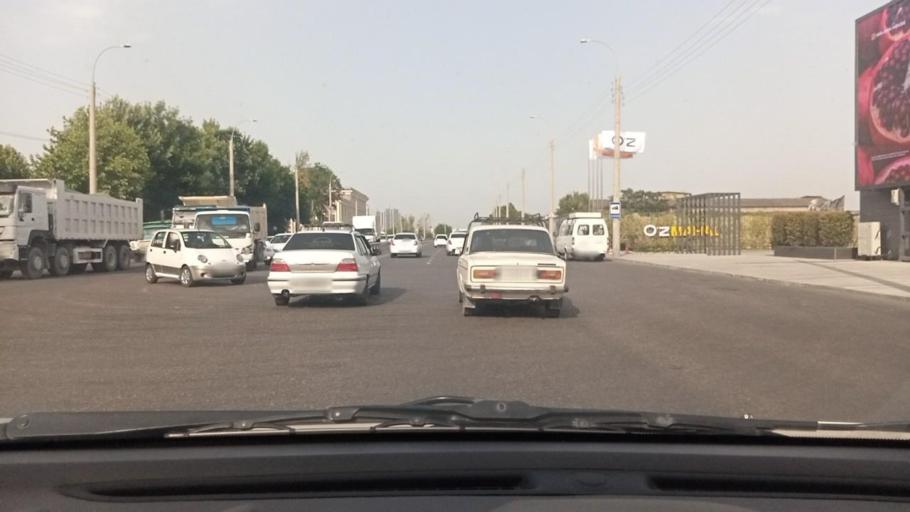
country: UZ
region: Toshkent
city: Salor
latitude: 41.3340
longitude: 69.3057
